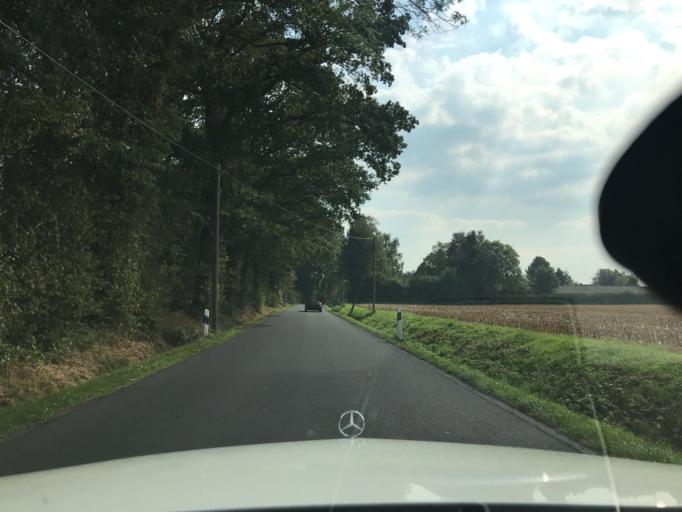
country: DE
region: North Rhine-Westphalia
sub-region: Regierungsbezirk Arnsberg
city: Werl
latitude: 51.5846
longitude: 7.8685
